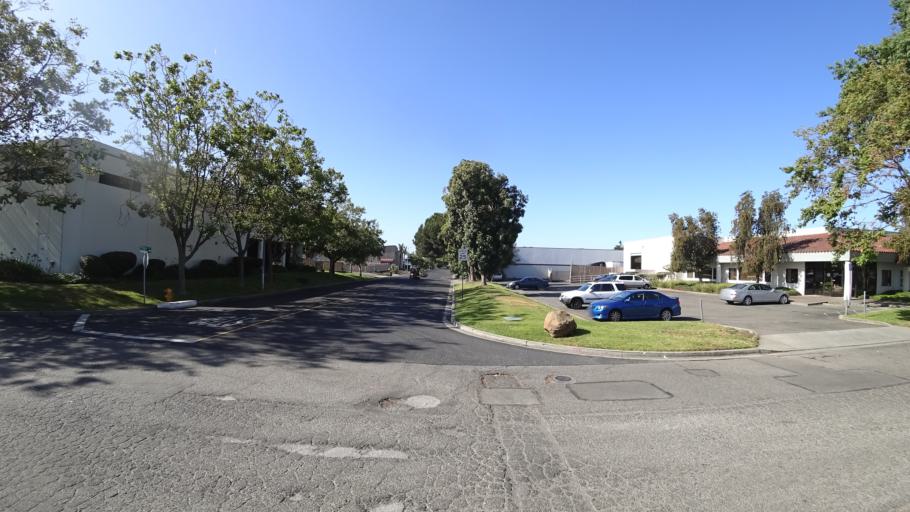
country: US
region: California
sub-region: Alameda County
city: San Lorenzo
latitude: 37.6445
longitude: -122.1315
